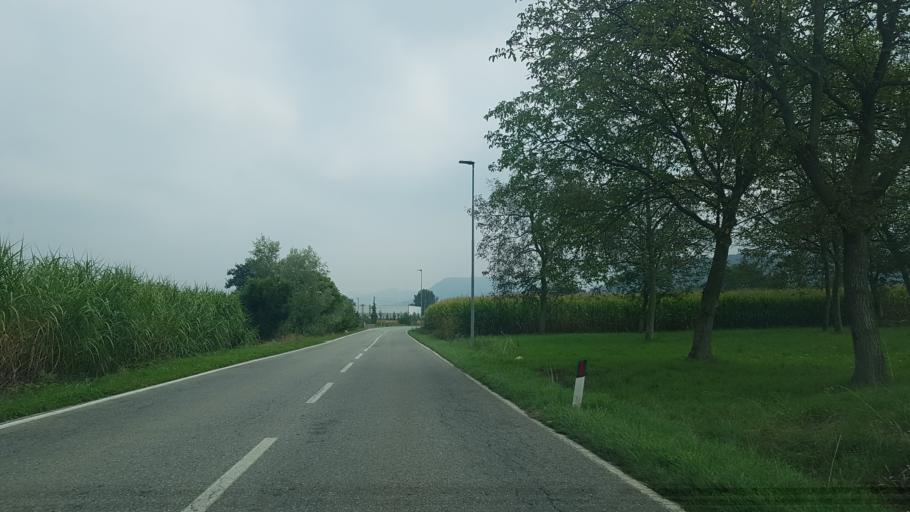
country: IT
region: Piedmont
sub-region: Provincia di Cuneo
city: Peveragno
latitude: 44.3304
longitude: 7.6286
